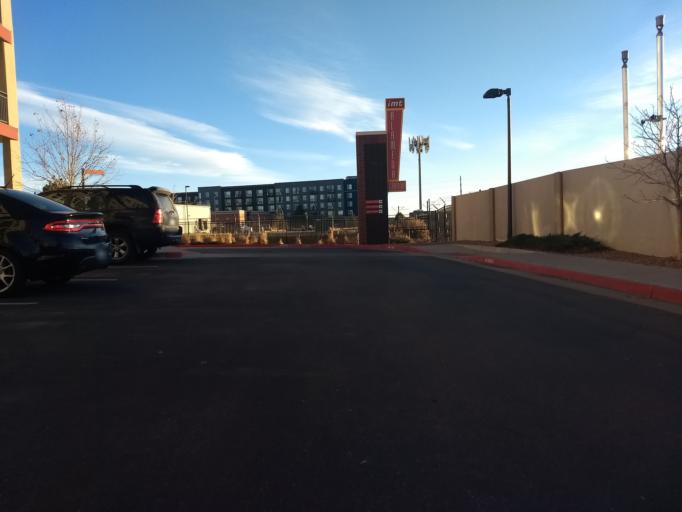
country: US
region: Colorado
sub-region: Denver County
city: Denver
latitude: 39.7116
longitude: -104.9946
